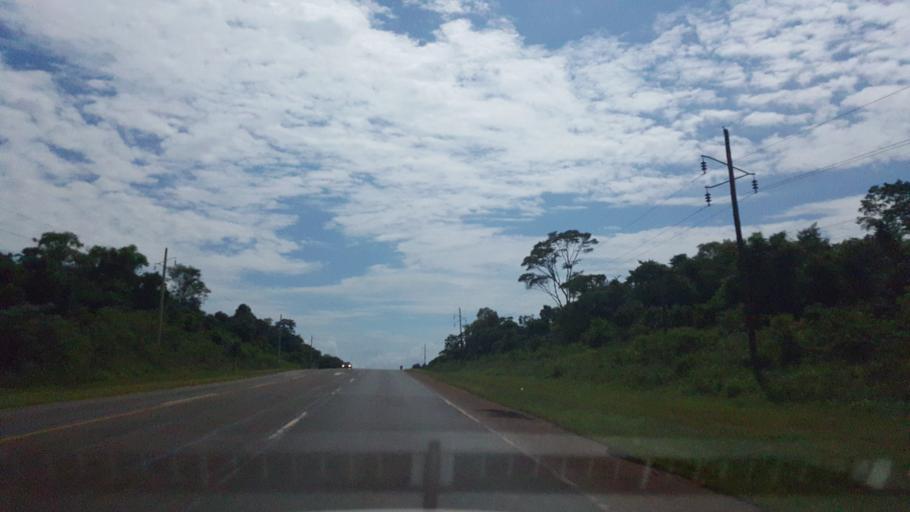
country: AR
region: Misiones
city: Capiovi
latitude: -26.8886
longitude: -55.0546
